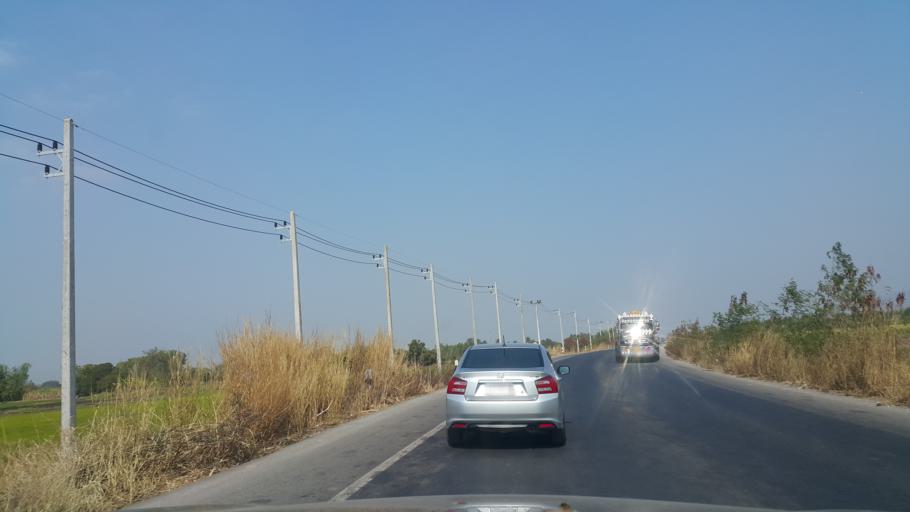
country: TH
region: Chaiyaphum
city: Phu Khiao
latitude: 16.3858
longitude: 102.1203
